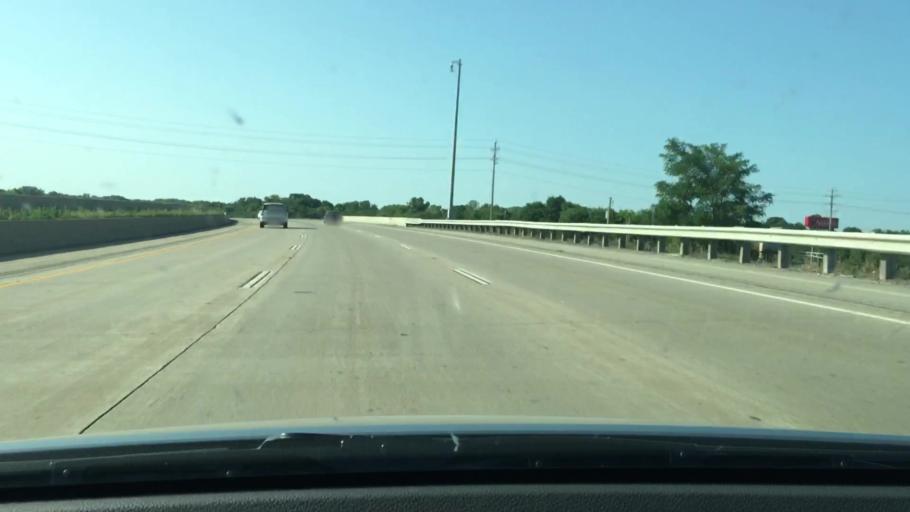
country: US
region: Wisconsin
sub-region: Winnebago County
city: Neenah
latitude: 44.1770
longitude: -88.4893
